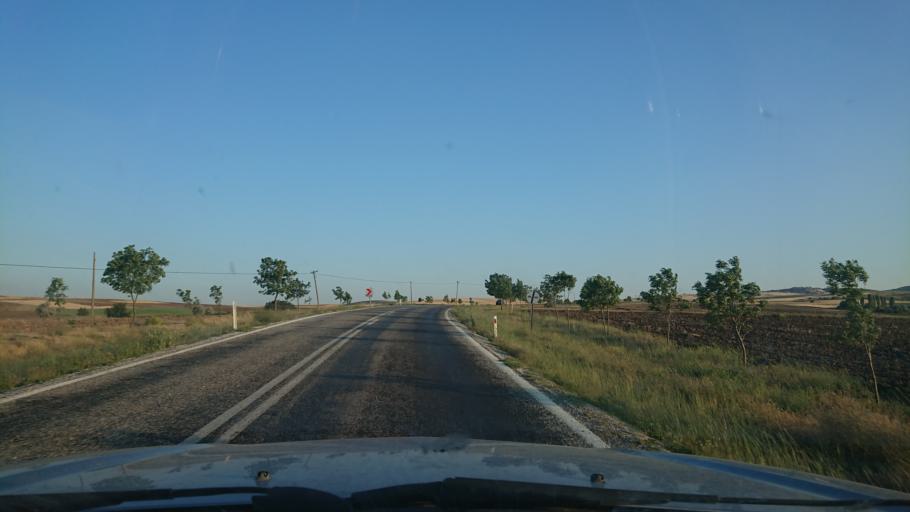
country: TR
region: Aksaray
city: Sariyahsi
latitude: 38.9500
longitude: 33.8389
